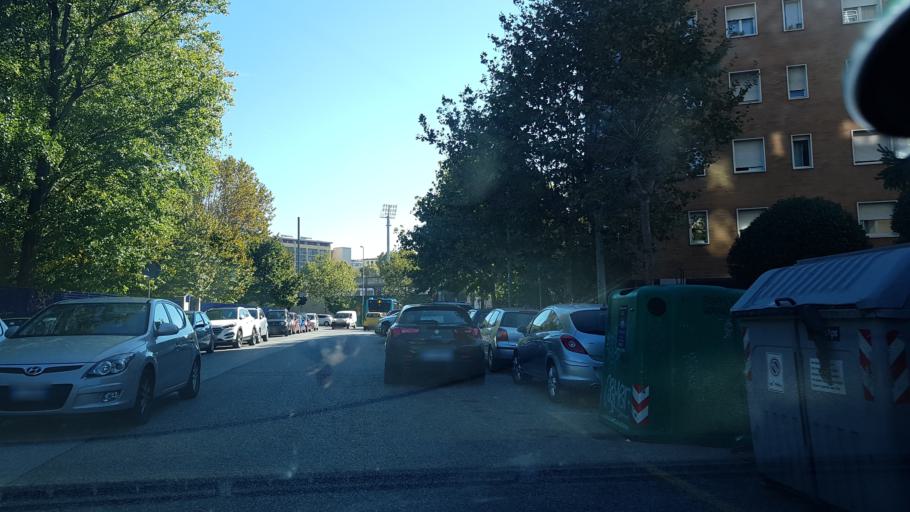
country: IT
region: Friuli Venezia Giulia
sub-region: Provincia di Trieste
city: Trieste
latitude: 45.6249
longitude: 13.7920
